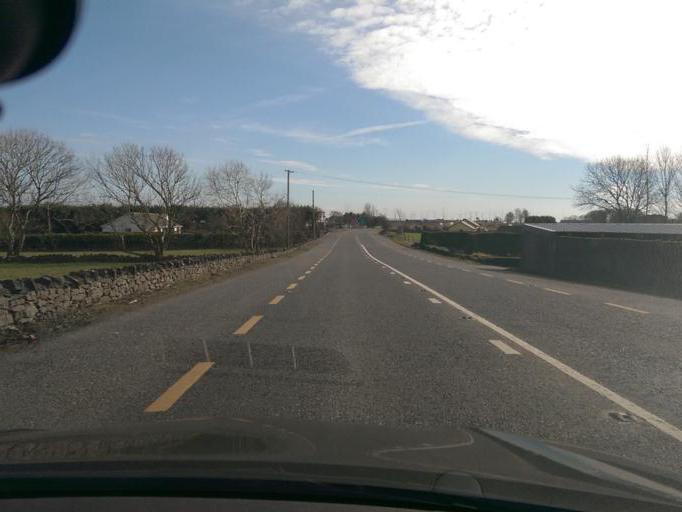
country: IE
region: Connaught
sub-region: County Galway
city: Oranmore
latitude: 53.3002
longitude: -8.9255
